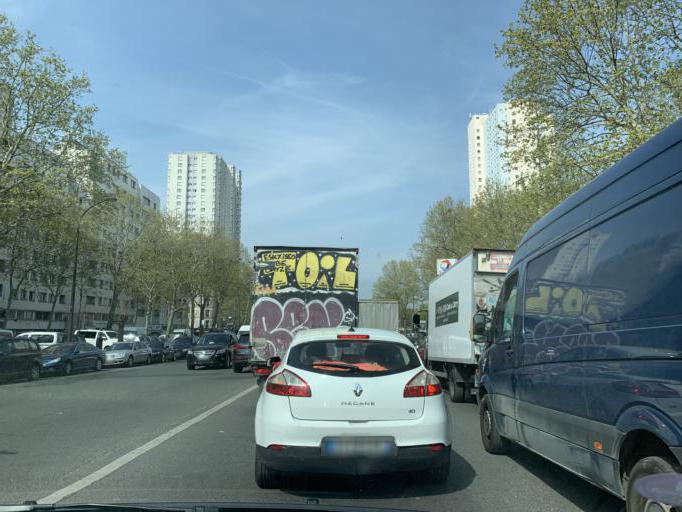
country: FR
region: Ile-de-France
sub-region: Paris
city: Saint-Ouen
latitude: 48.8956
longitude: 2.3595
